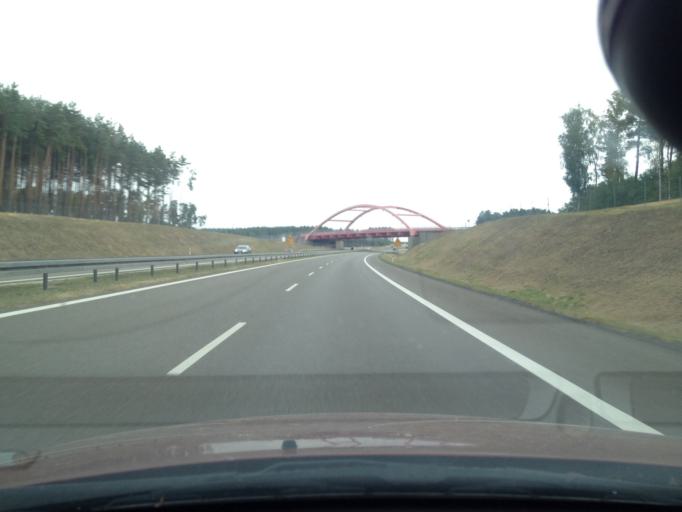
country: PL
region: Lubusz
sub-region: Powiat zielonogorski
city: Sulechow
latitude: 52.1498
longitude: 15.5787
